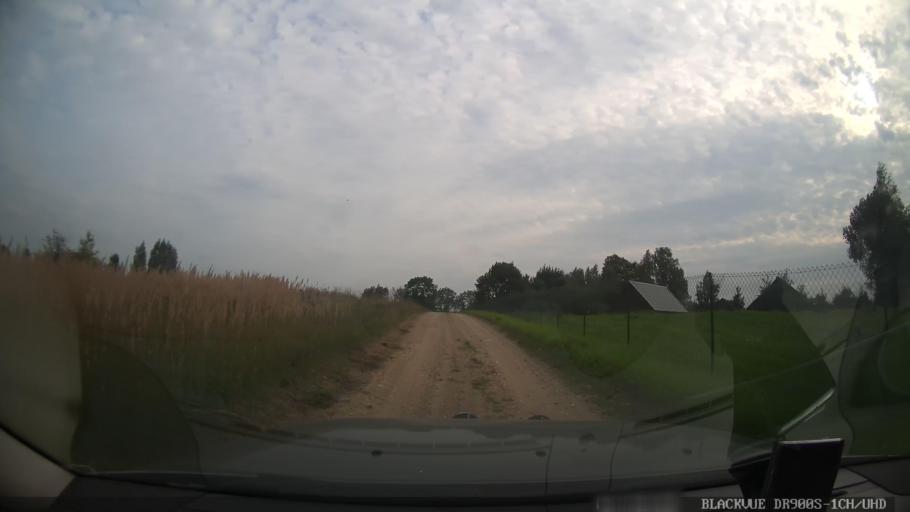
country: BY
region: Grodnenskaya
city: Ashmyany
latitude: 54.5316
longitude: 25.6701
